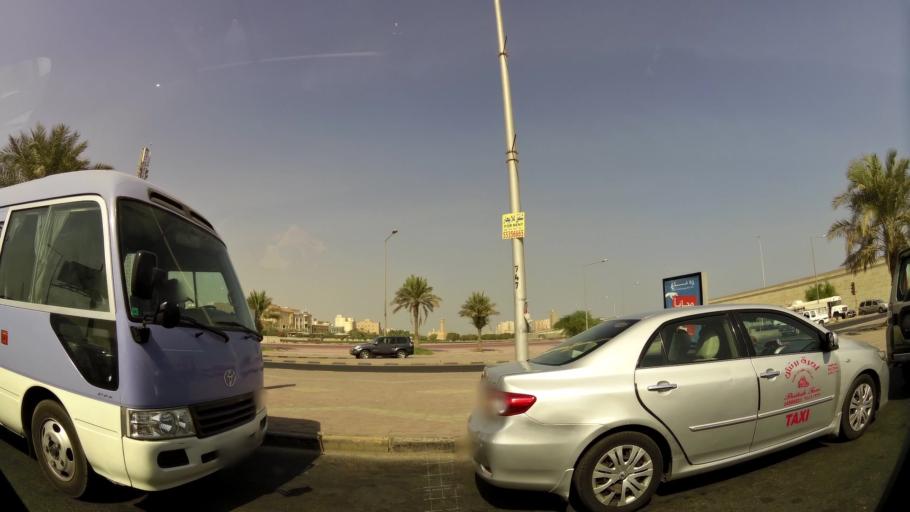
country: KW
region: Al Ahmadi
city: Al Fahahil
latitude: 29.0908
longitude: 48.1149
